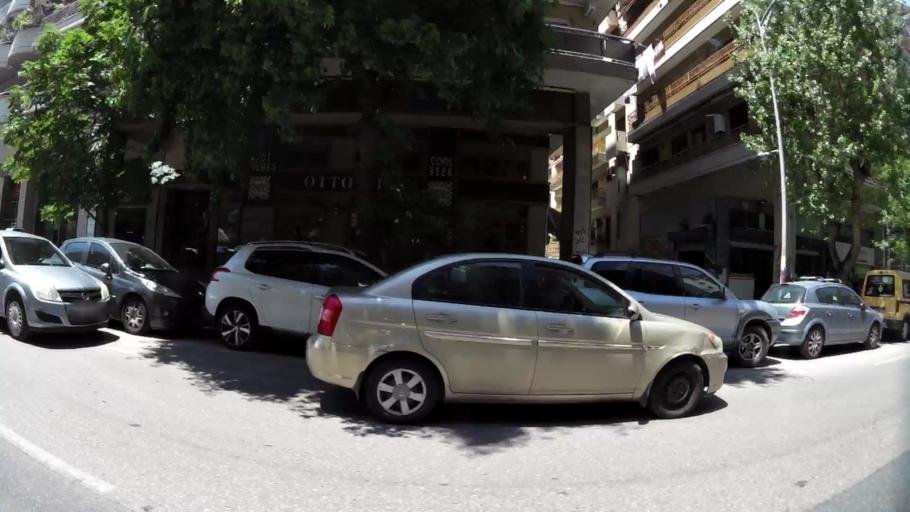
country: GR
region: Central Macedonia
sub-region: Nomos Thessalonikis
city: Triandria
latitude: 40.6180
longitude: 22.9545
